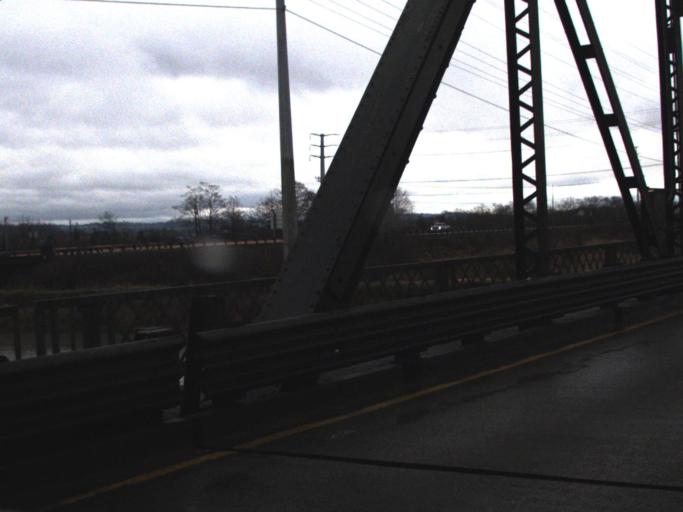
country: US
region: Washington
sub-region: Snohomish County
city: Marysville
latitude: 48.0359
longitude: -122.1825
